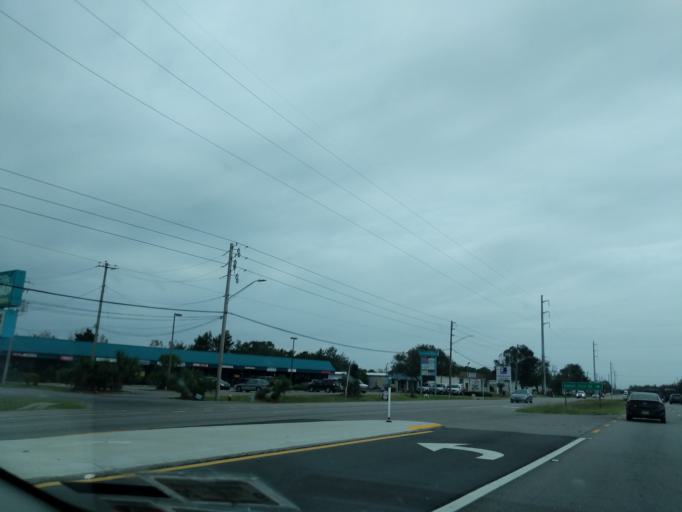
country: US
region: Florida
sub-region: Santa Rosa County
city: Oriole Beach
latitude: 30.3846
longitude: -87.0960
